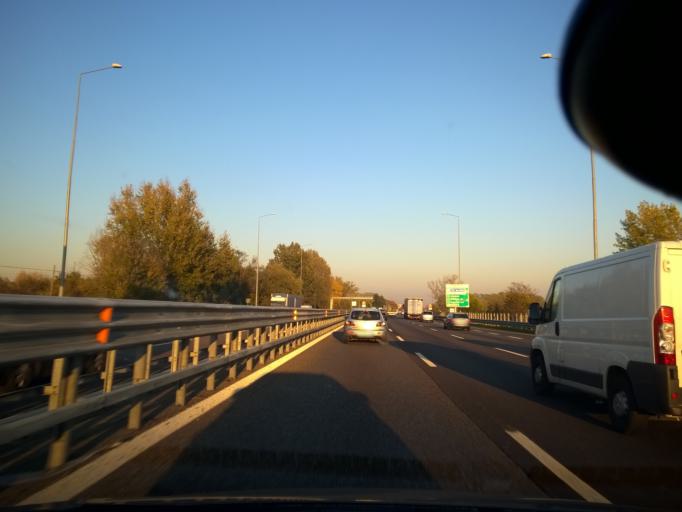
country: IT
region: Lombardy
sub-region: Citta metropolitana di Milano
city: Fizzonasco
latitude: 45.3897
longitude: 9.1839
